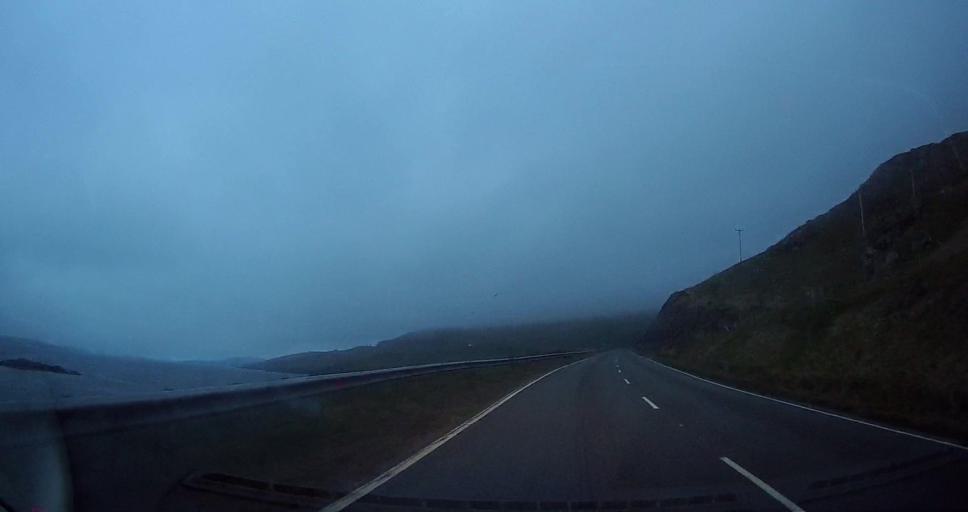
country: GB
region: Scotland
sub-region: Shetland Islands
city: Sandwick
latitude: 60.0326
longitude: -1.2337
